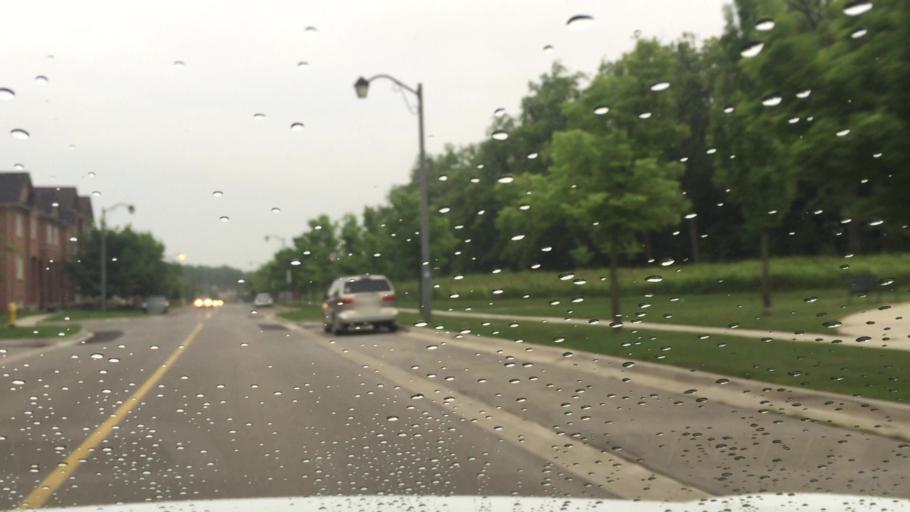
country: CA
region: Ontario
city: Markham
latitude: 43.8982
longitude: -79.2203
